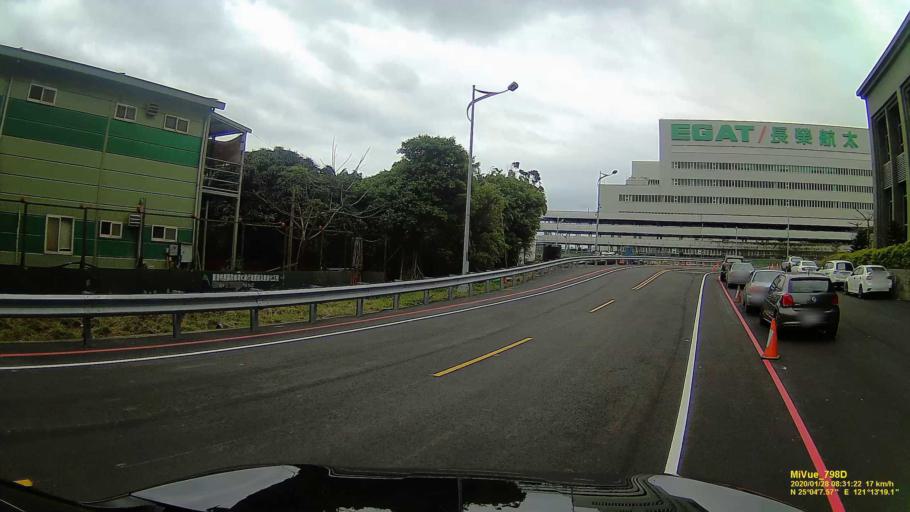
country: TW
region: Taiwan
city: Taoyuan City
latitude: 25.0689
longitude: 121.2216
